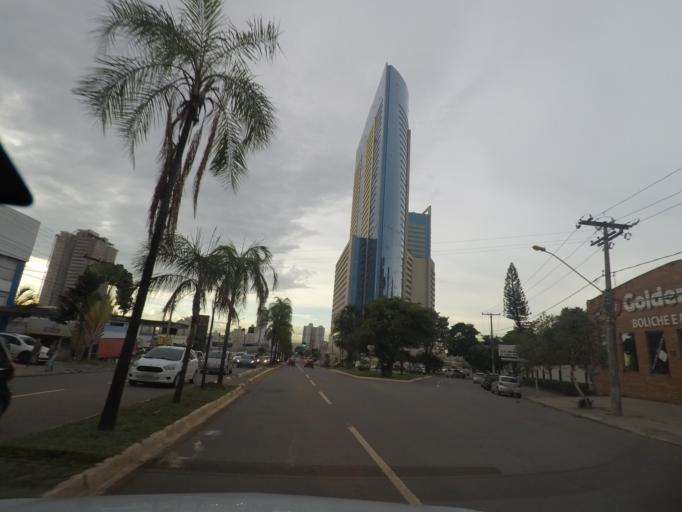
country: BR
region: Goias
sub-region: Goiania
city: Goiania
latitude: -16.6984
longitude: -49.2690
